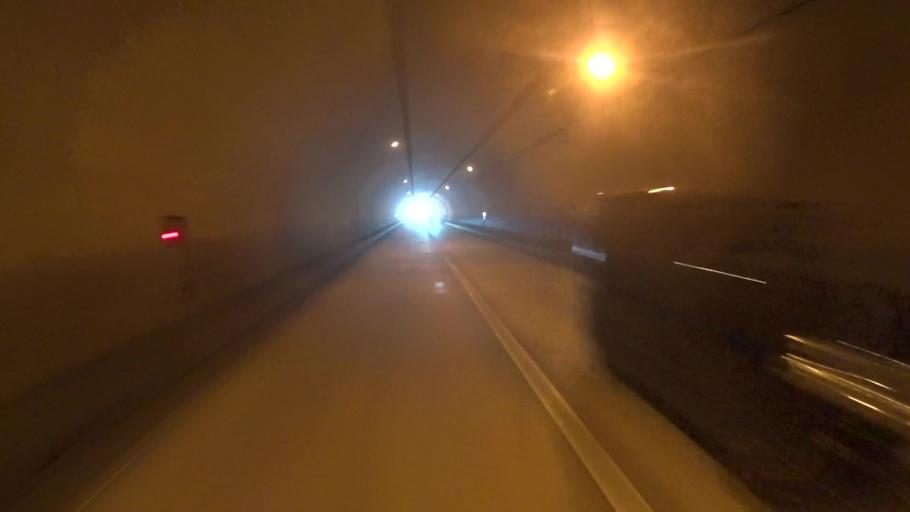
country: JP
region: Kyoto
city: Miyazu
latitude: 35.6796
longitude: 135.2820
